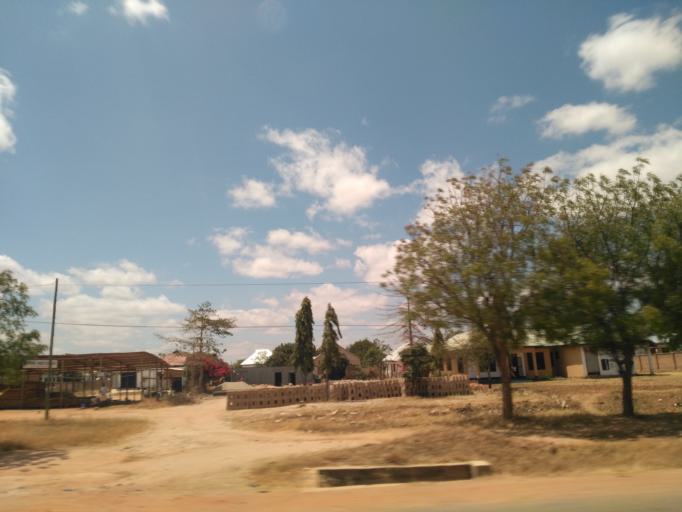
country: TZ
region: Dodoma
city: Kisasa
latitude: -6.1626
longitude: 35.7901
